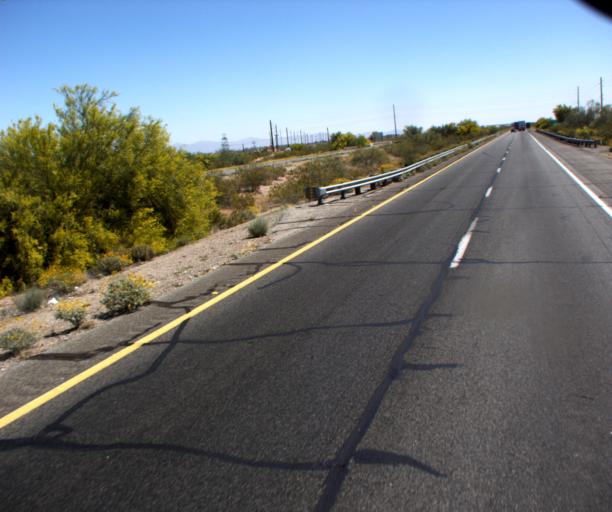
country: US
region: Arizona
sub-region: Maricopa County
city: Buckeye
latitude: 33.4934
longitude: -112.9197
